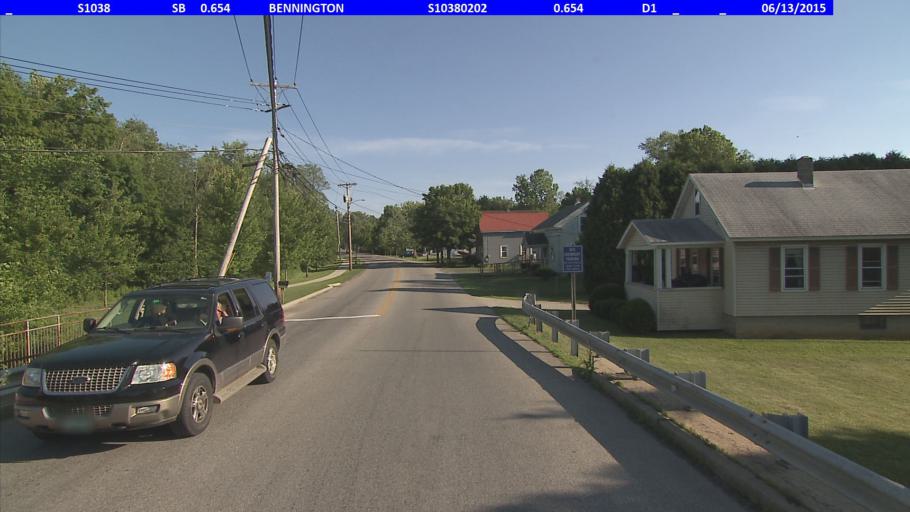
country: US
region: Vermont
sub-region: Bennington County
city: Bennington
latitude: 42.8938
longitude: -73.1933
